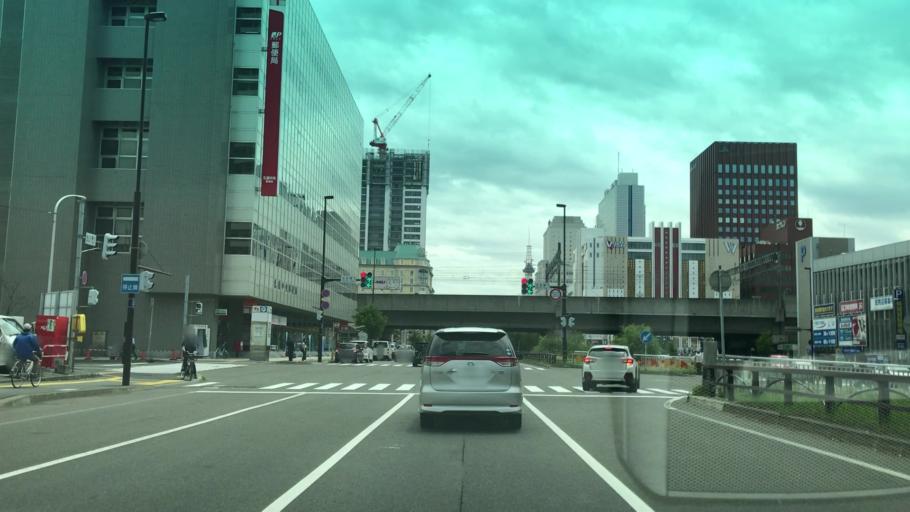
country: JP
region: Hokkaido
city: Sapporo
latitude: 43.0701
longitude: 141.3550
